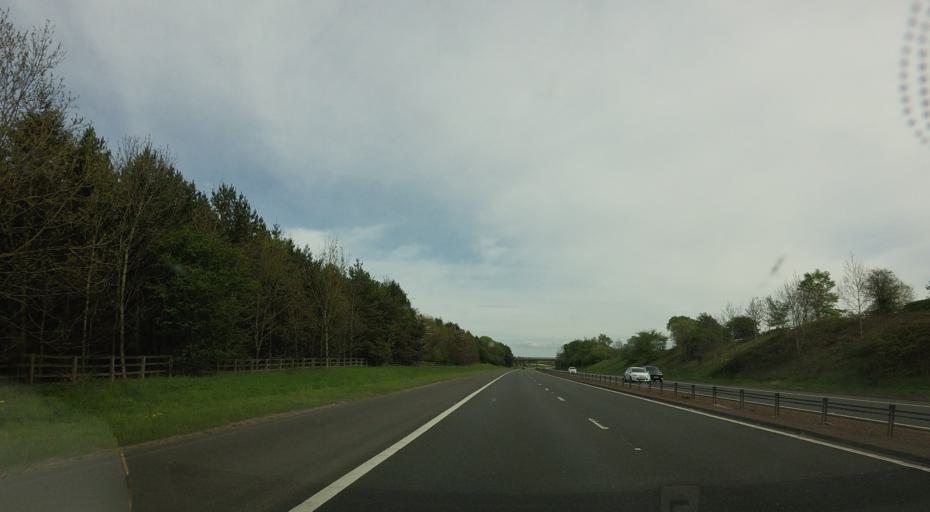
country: GB
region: Scotland
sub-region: West Lothian
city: Broxburn
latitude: 55.9766
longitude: -3.4780
